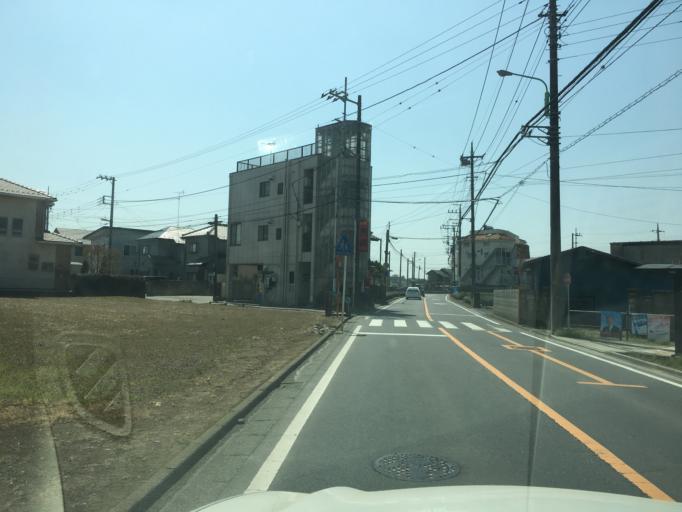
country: JP
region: Saitama
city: Sayama
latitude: 35.8367
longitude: 139.4367
